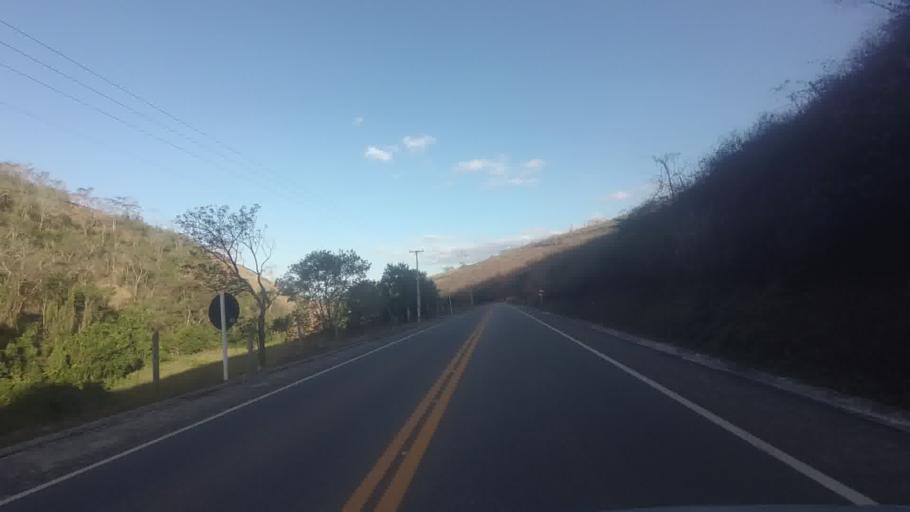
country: BR
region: Espirito Santo
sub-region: Cachoeiro De Itapemirim
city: Cachoeiro de Itapemirim
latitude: -20.8265
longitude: -41.1933
